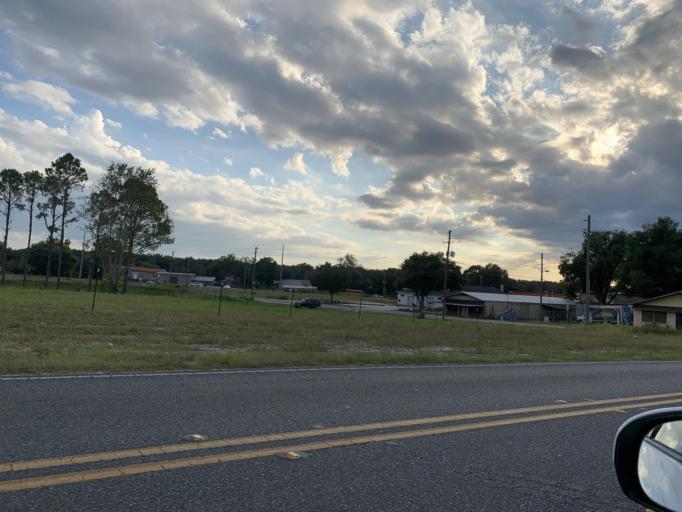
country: US
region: Florida
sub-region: Marion County
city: Silver Springs Shores
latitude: 29.1500
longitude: -82.0696
